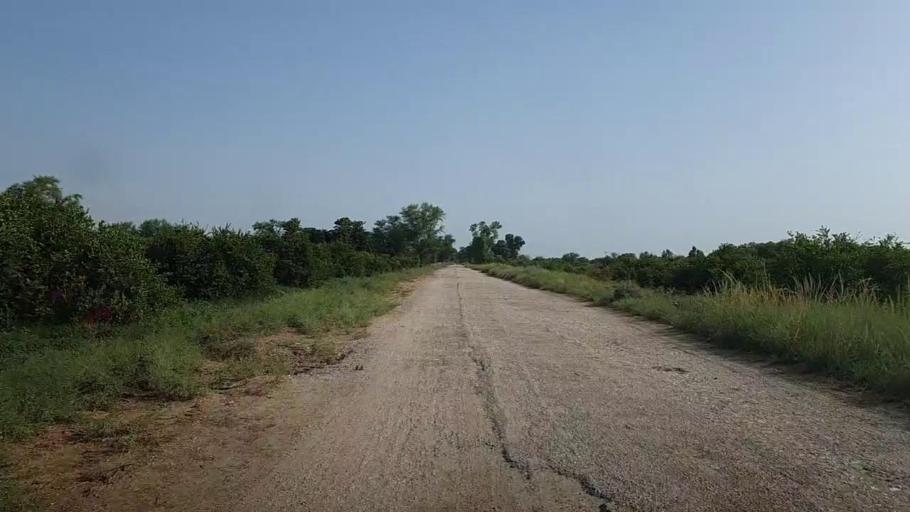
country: PK
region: Sindh
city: Karaundi
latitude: 26.8605
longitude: 68.3309
